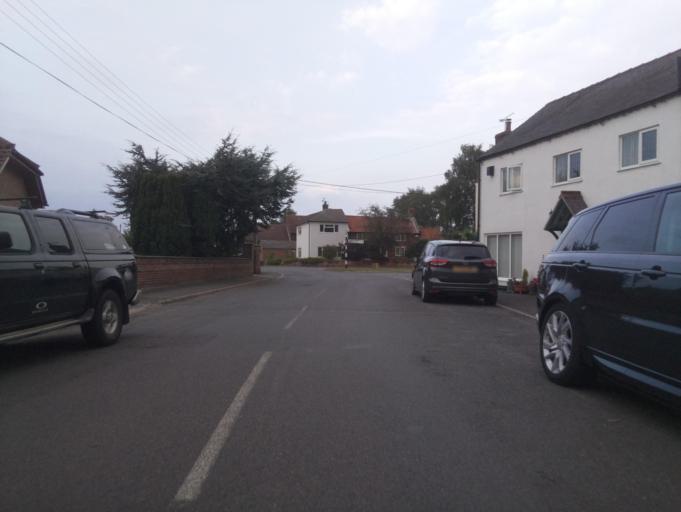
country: GB
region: England
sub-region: Lincolnshire
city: Skellingthorpe
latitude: 53.1314
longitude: -0.6384
